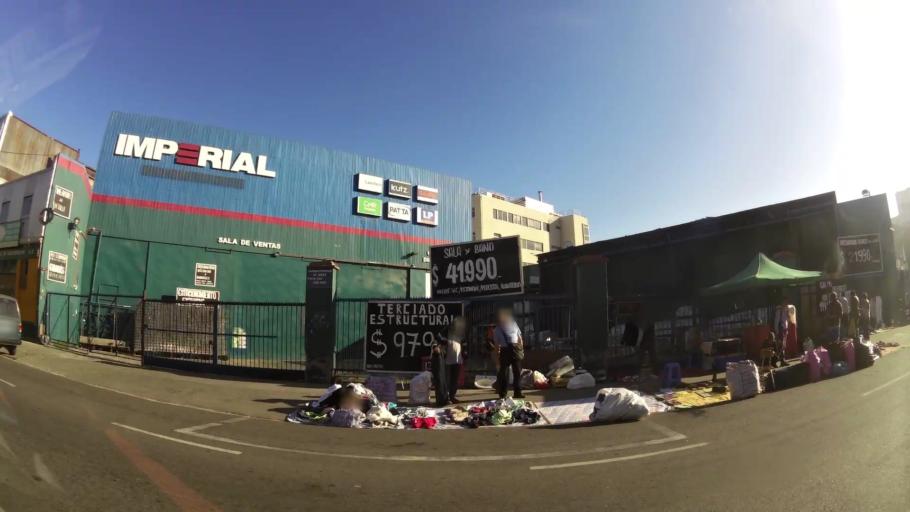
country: CL
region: Valparaiso
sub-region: Provincia de Valparaiso
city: Valparaiso
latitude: -33.0508
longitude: -71.6043
